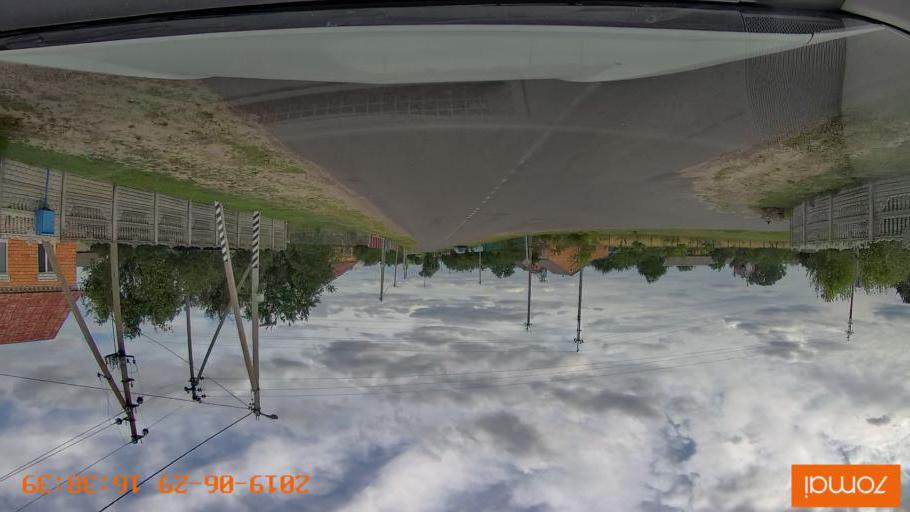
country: BY
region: Brest
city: Luninyets
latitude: 52.2345
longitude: 27.0153
